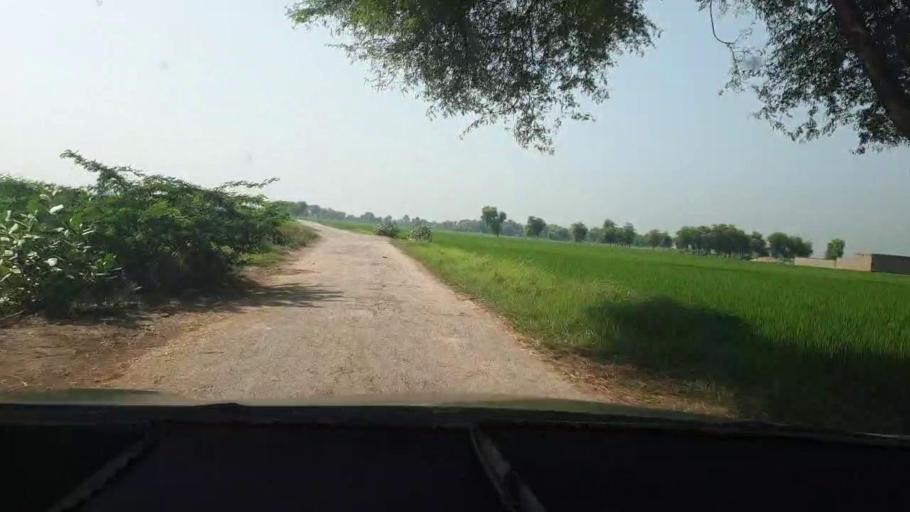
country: PK
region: Sindh
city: Kambar
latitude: 27.5761
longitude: 68.0556
